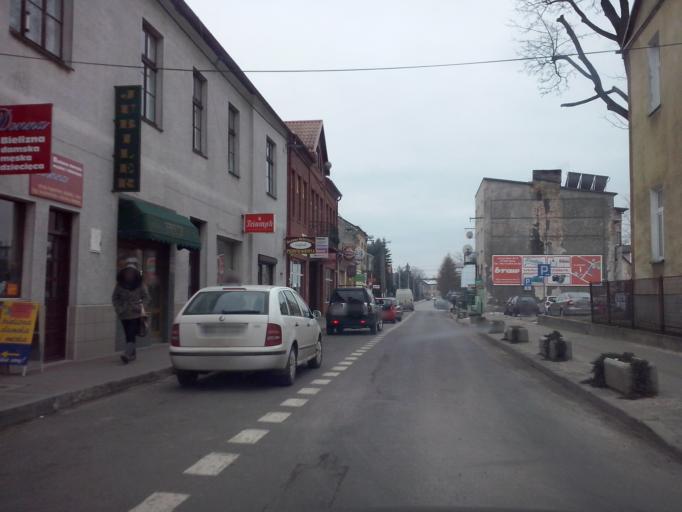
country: PL
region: Subcarpathian Voivodeship
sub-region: Powiat nizanski
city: Nisko
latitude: 50.5176
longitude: 22.1445
